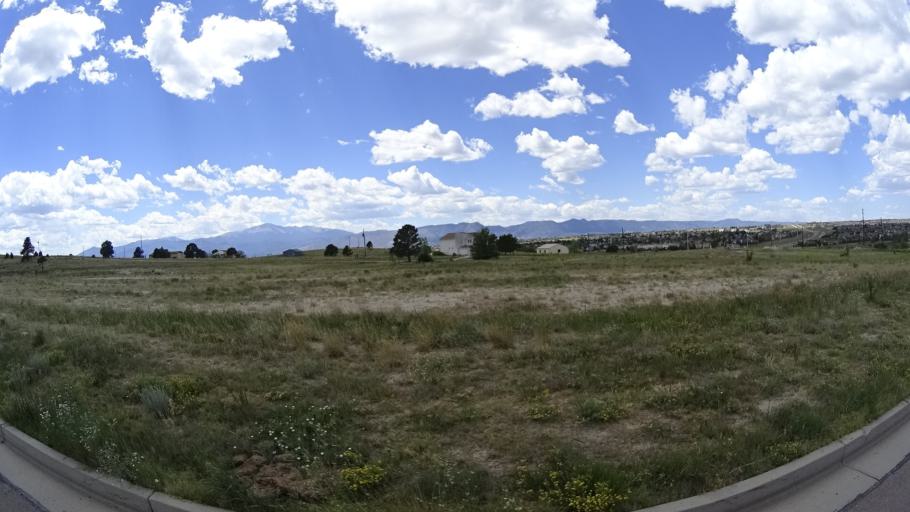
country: US
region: Colorado
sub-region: El Paso County
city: Black Forest
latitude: 38.9450
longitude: -104.7149
